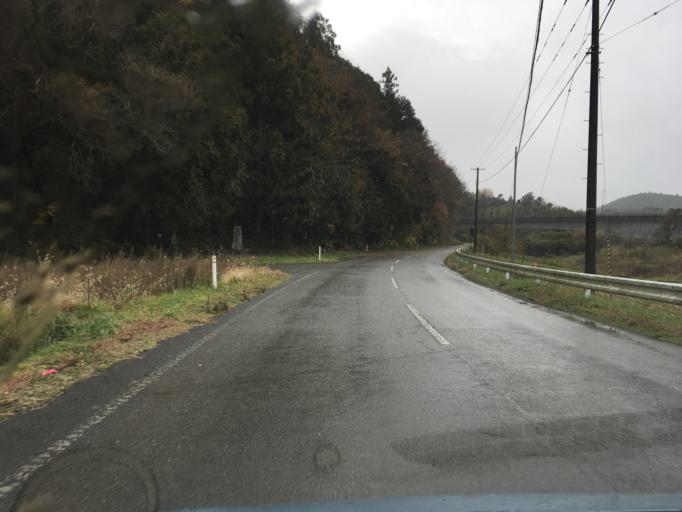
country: JP
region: Iwate
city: Ichinoseki
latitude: 38.7968
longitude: 141.2491
